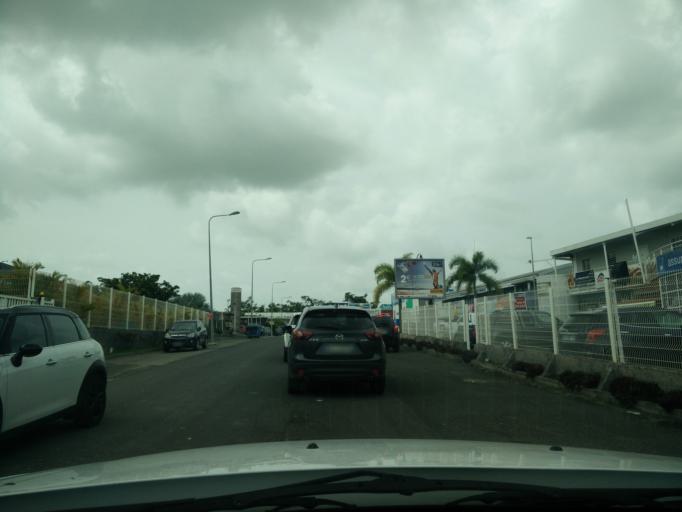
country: GP
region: Guadeloupe
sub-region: Guadeloupe
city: Baie-Mahault
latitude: 16.2462
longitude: -61.5708
